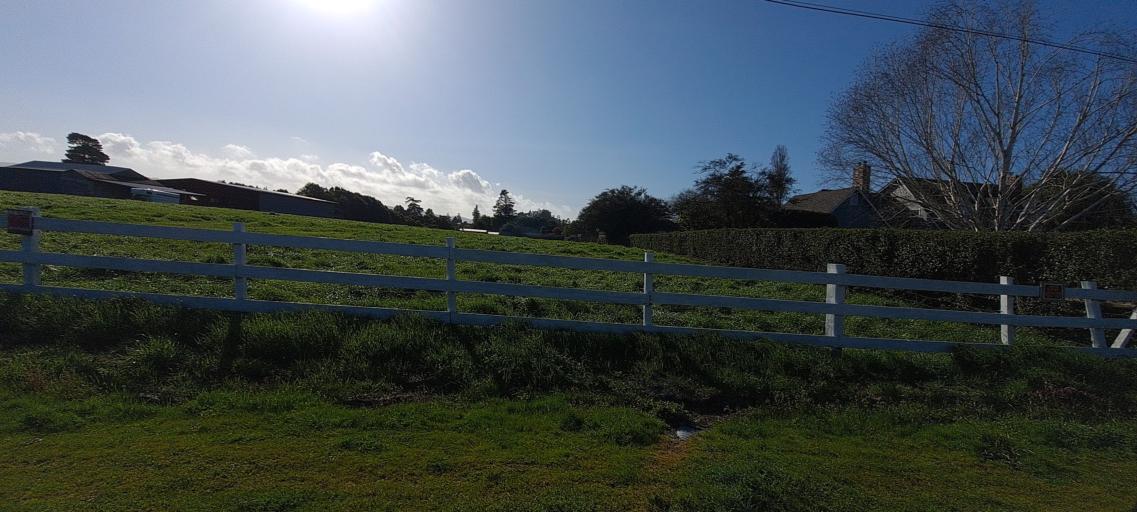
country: US
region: California
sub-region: Humboldt County
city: Fortuna
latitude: 40.5756
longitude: -124.1355
